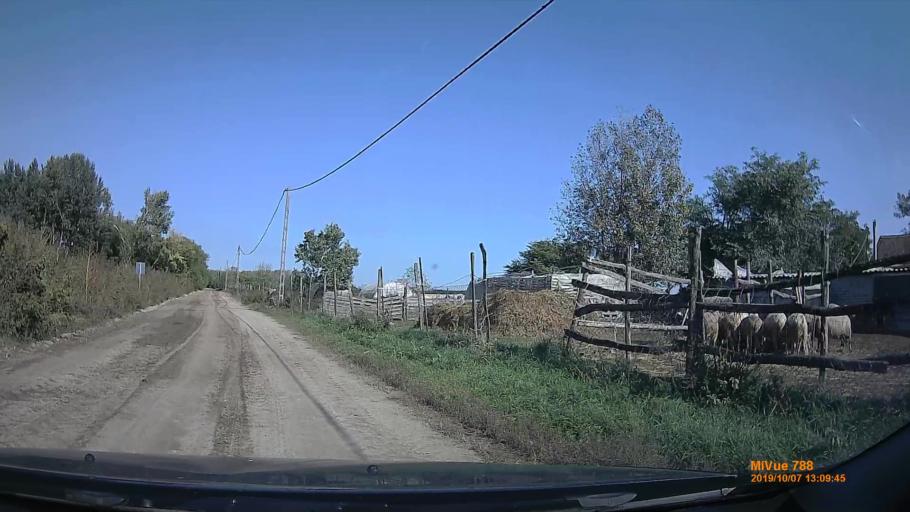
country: HU
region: Jasz-Nagykun-Szolnok
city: Cserkeszolo
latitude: 46.8767
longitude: 20.1841
